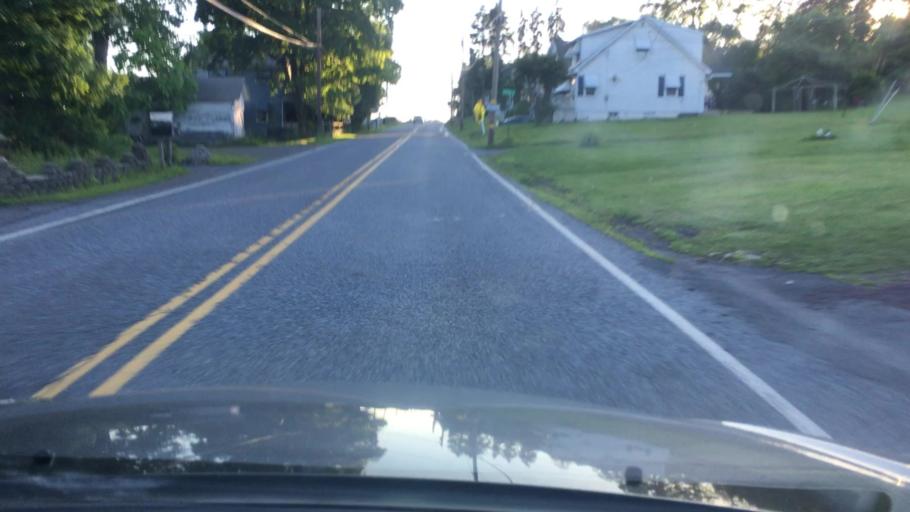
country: US
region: Pennsylvania
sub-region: Luzerne County
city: Harleigh
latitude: 41.0211
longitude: -75.9737
